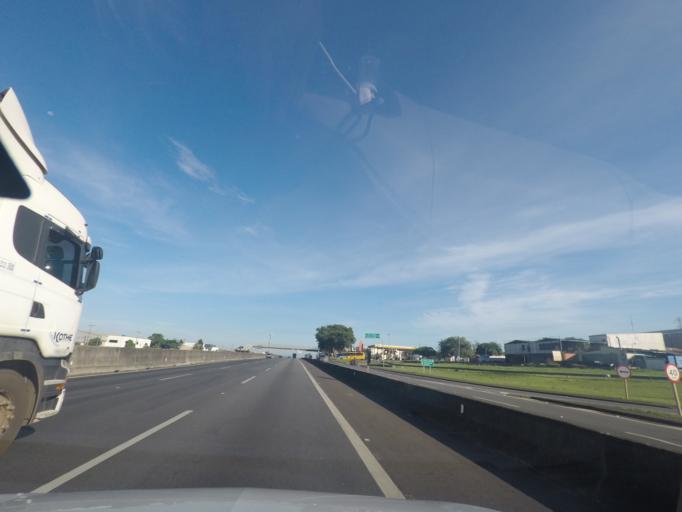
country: BR
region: Sao Paulo
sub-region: Nova Odessa
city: Nova Odessa
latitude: -22.7531
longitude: -47.2584
